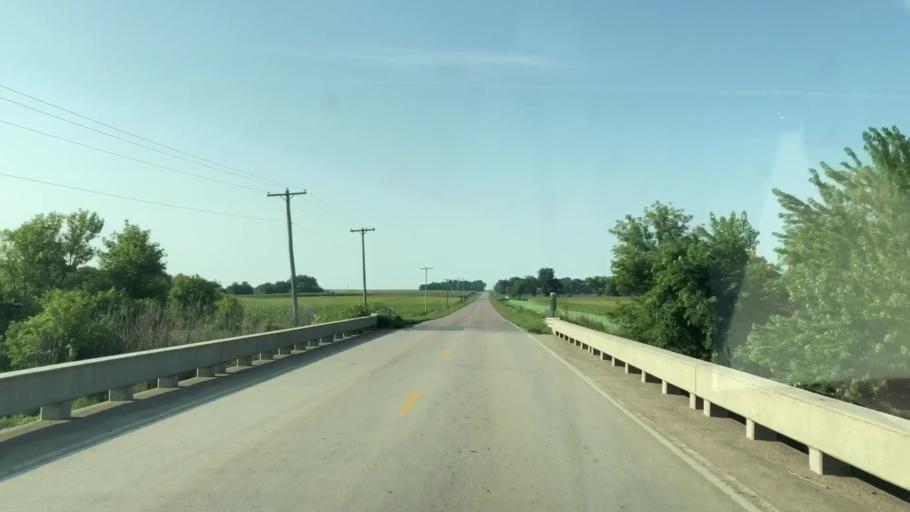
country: US
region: Iowa
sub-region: Lyon County
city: George
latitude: 43.2486
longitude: -96.0004
